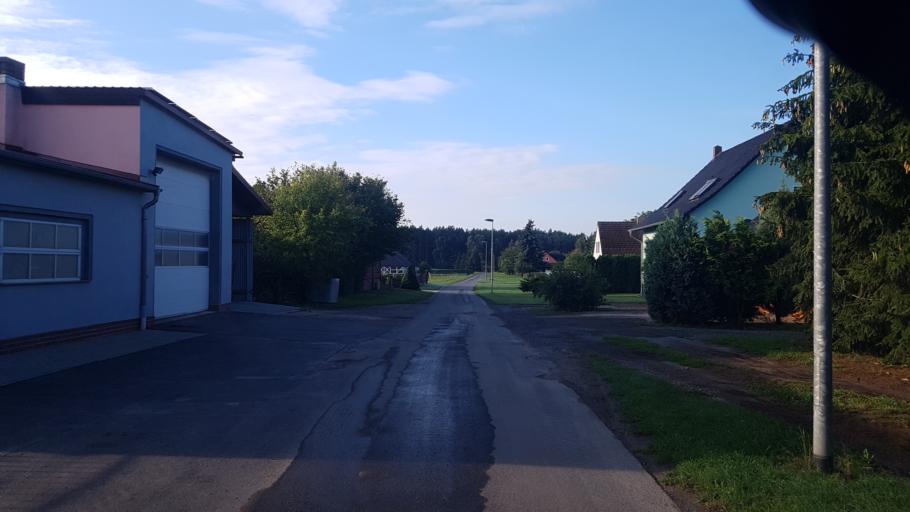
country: DE
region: Brandenburg
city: Bronkow
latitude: 51.6754
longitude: 13.8920
